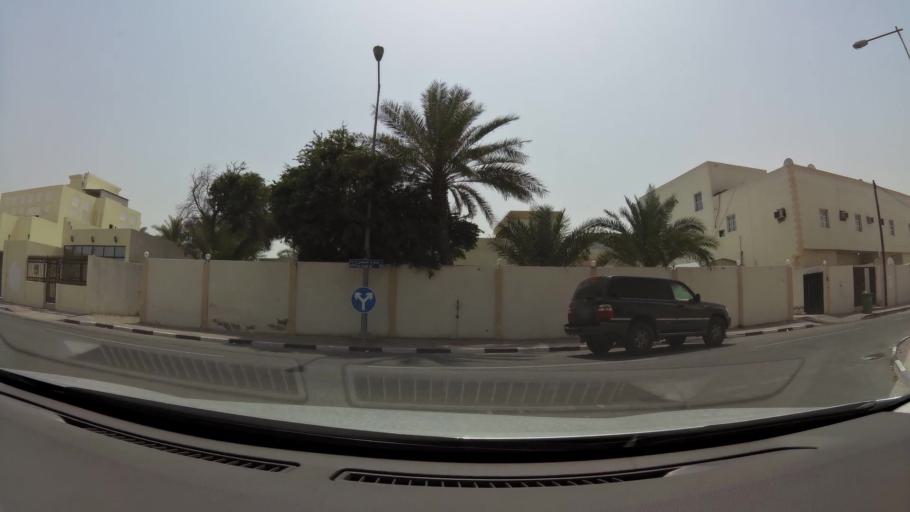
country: QA
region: Baladiyat ar Rayyan
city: Ar Rayyan
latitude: 25.2477
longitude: 51.4284
